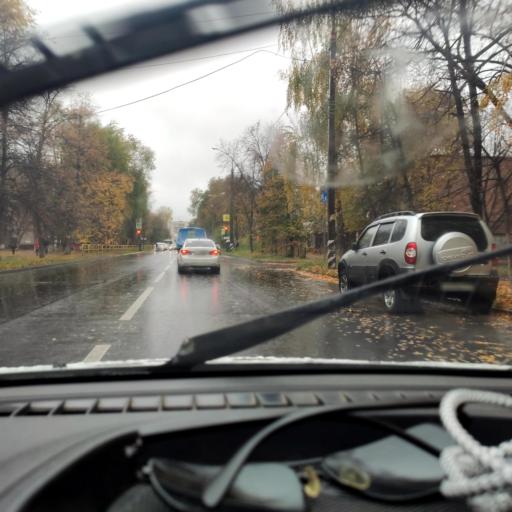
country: RU
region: Samara
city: Tol'yatti
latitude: 53.5238
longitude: 49.4281
